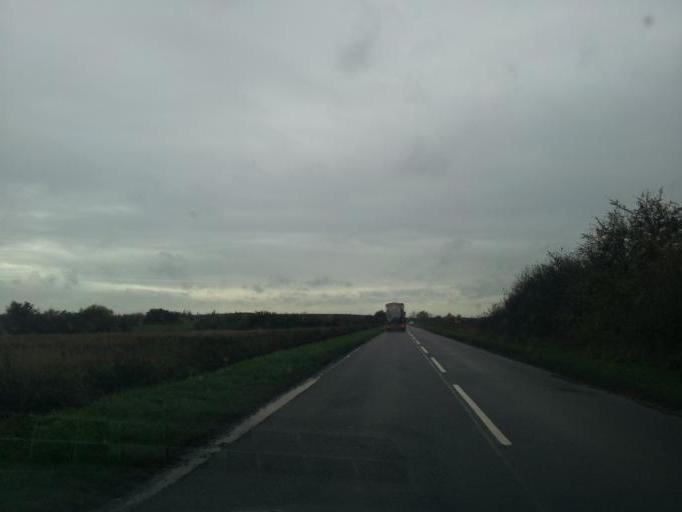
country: GB
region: England
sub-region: Nottinghamshire
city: Newark on Trent
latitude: 53.0484
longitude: -0.7824
